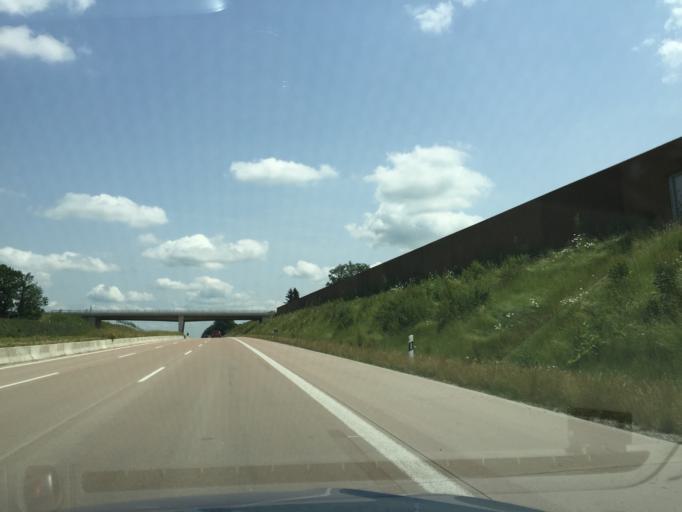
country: DE
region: Bavaria
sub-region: Swabia
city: Rettenbach
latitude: 48.4335
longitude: 10.3401
